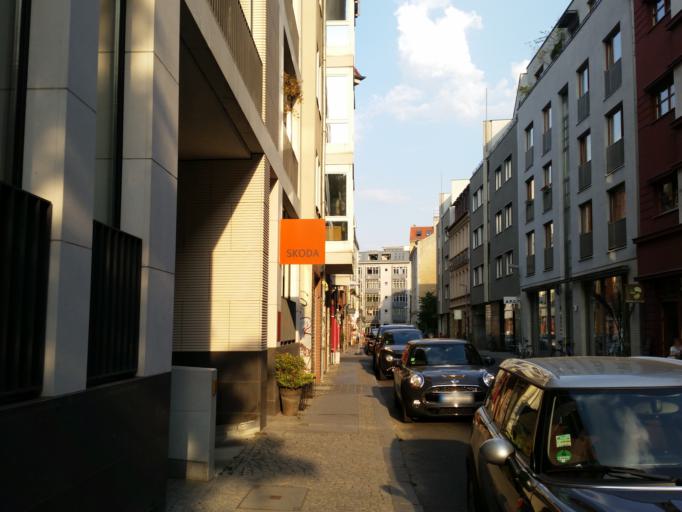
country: DE
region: Berlin
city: Berlin
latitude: 52.5274
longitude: 13.4060
